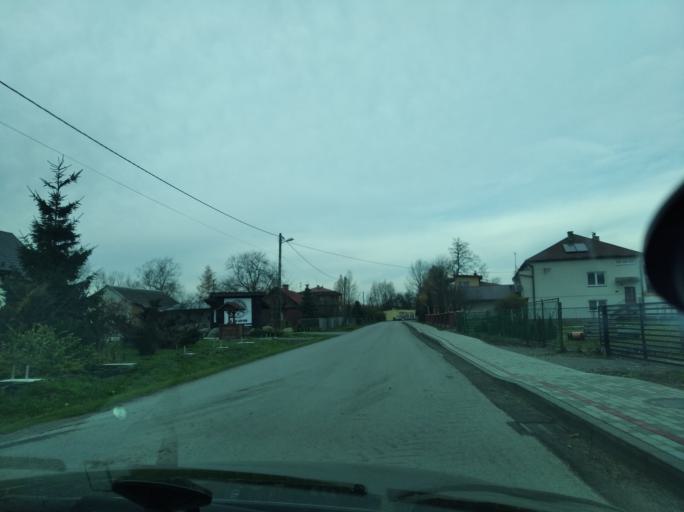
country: PL
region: Subcarpathian Voivodeship
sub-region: Powiat przeworski
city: Grzeska
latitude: 50.0856
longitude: 22.4465
